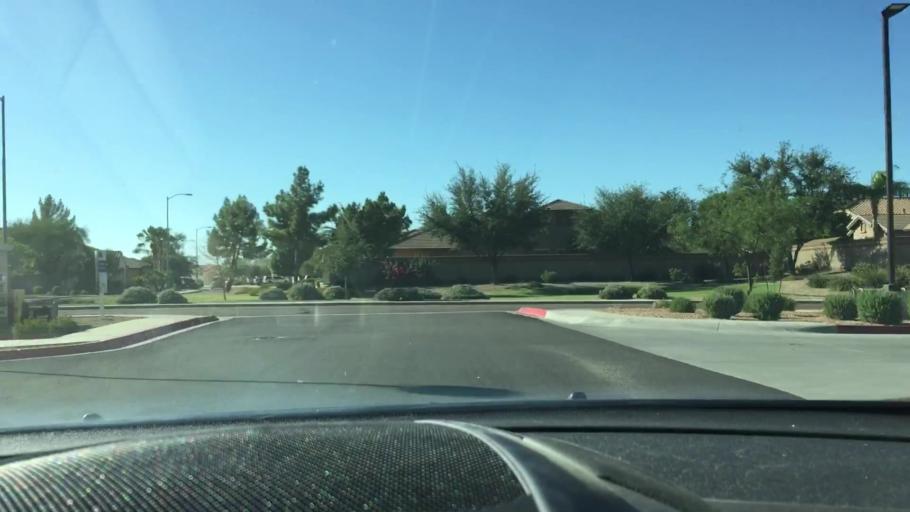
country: US
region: Arizona
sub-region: Maricopa County
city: Sun City
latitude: 33.6708
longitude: -112.2409
